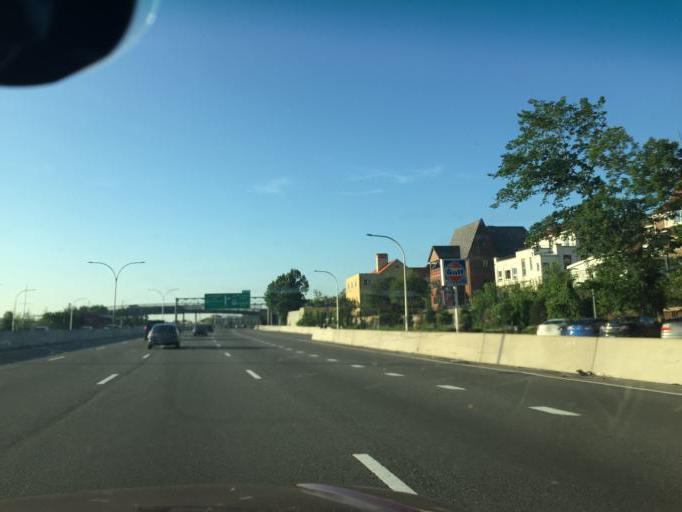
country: US
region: New York
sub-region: Bronx
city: The Bronx
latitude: 40.7676
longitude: -73.8648
